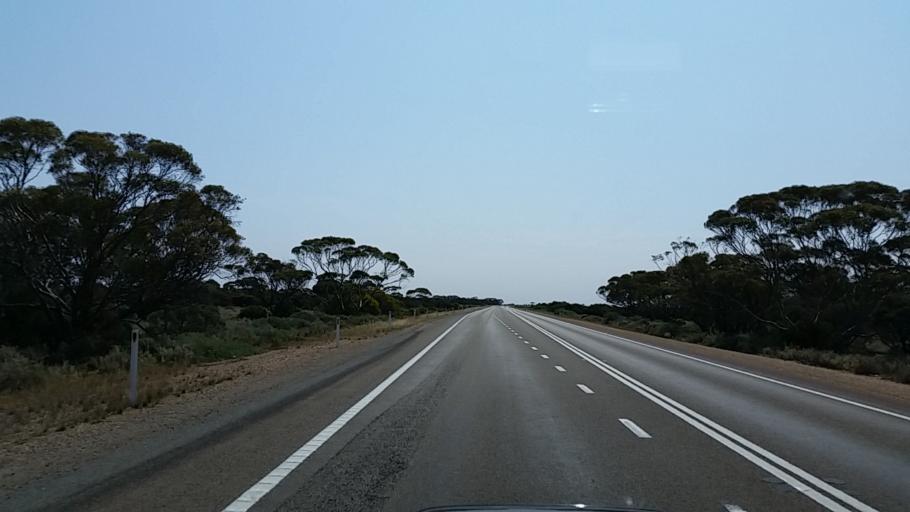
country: AU
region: South Australia
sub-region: Port Pirie City and Dists
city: Port Pirie
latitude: -32.9836
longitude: 137.9851
